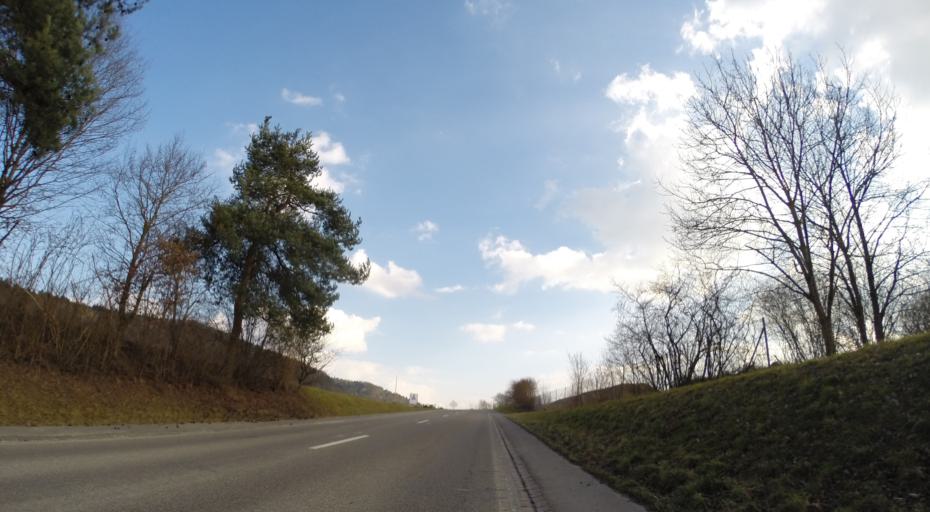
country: CH
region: Thurgau
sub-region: Frauenfeld District
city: Diessenhofen
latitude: 47.6498
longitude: 8.7857
